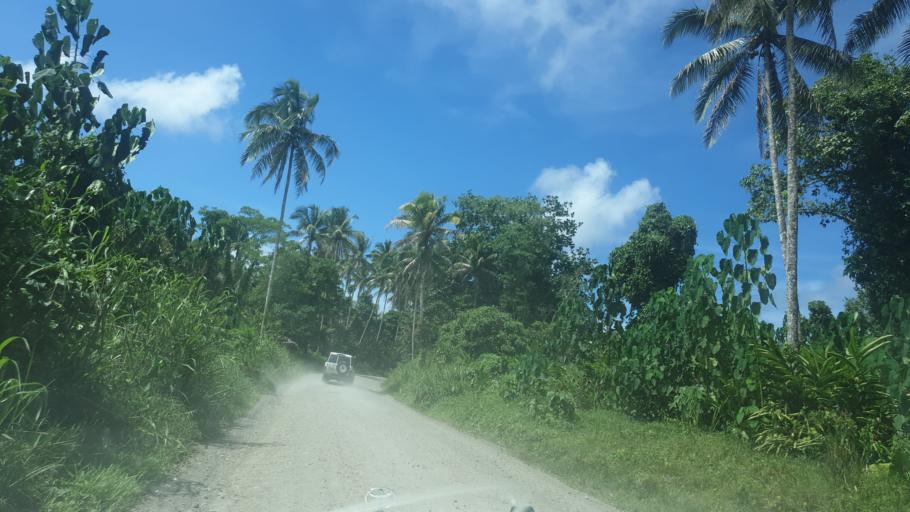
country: PG
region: Bougainville
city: Panguna
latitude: -6.7386
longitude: 155.6727
